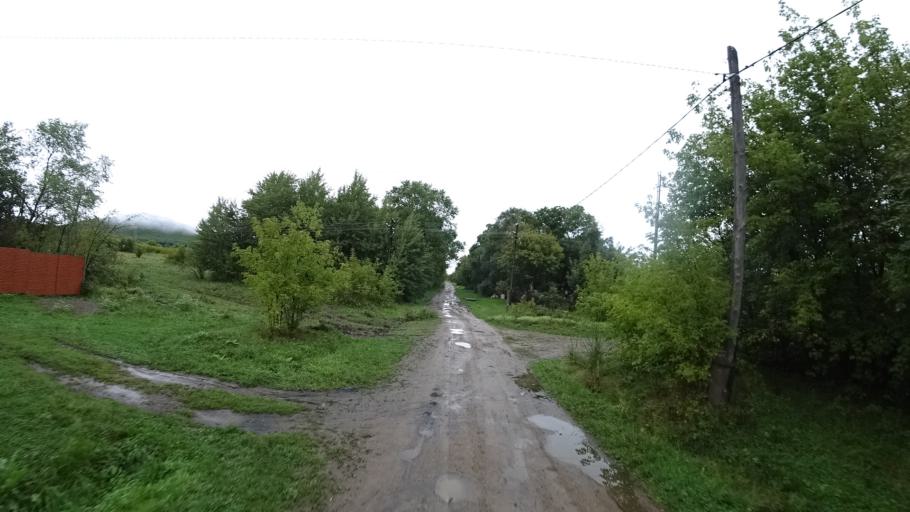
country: RU
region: Primorskiy
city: Monastyrishche
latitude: 44.2524
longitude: 132.4237
